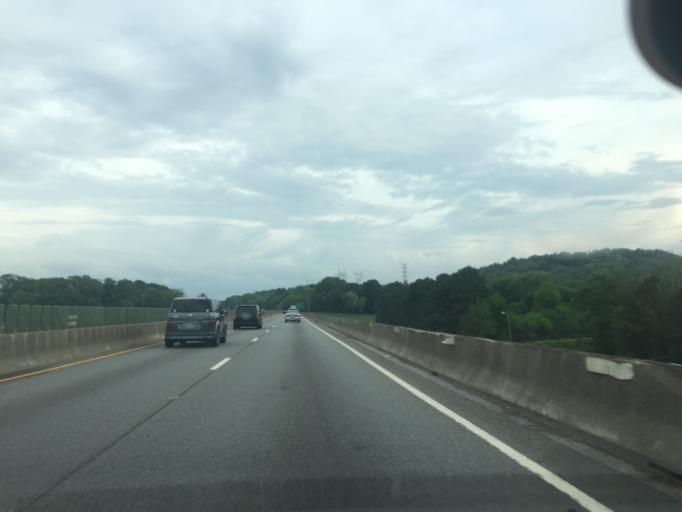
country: US
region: Tennessee
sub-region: Hamilton County
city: East Chattanooga
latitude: 35.0983
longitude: -85.2277
